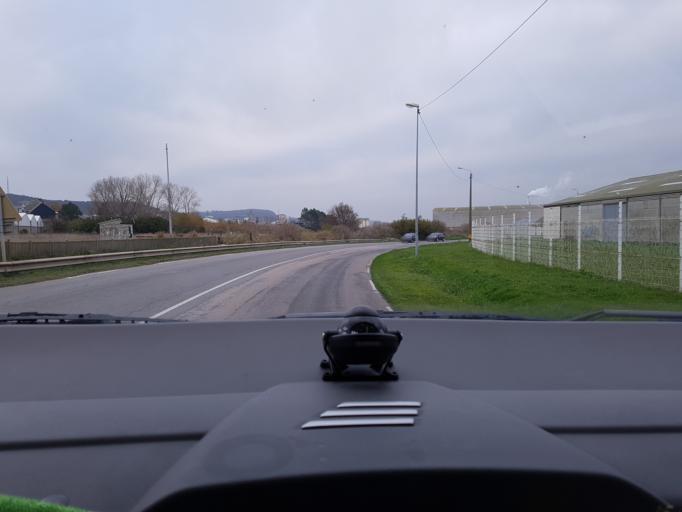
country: FR
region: Picardie
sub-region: Departement de la Somme
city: Mers-les-Bains
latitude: 50.0628
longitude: 1.3825
